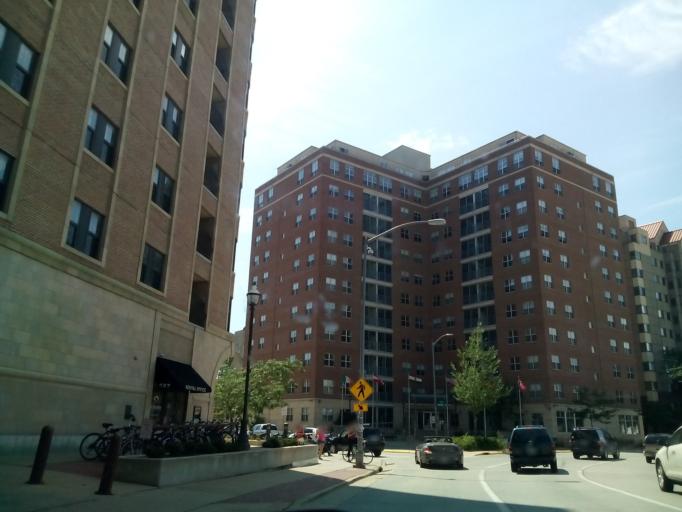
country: US
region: Wisconsin
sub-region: Dane County
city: Madison
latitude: 43.0733
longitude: -89.3937
